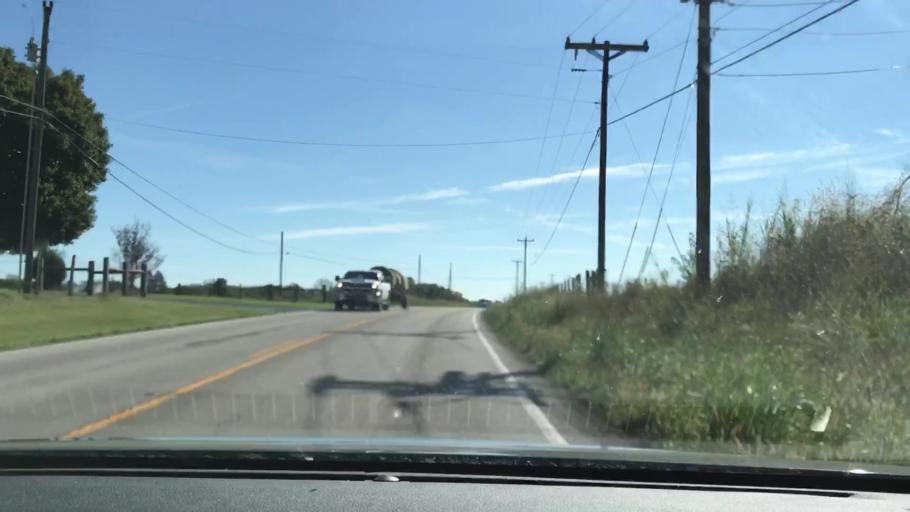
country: US
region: Kentucky
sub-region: Christian County
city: Hopkinsville
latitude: 36.8604
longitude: -87.4339
